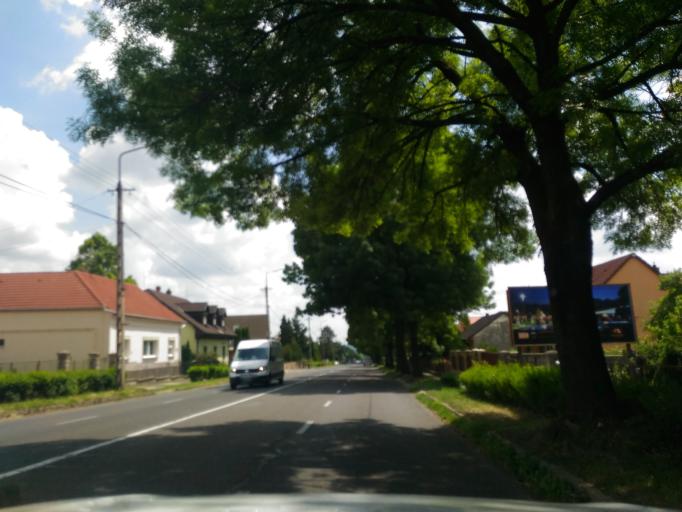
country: HU
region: Baranya
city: Pecs
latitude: 46.1063
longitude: 18.2637
